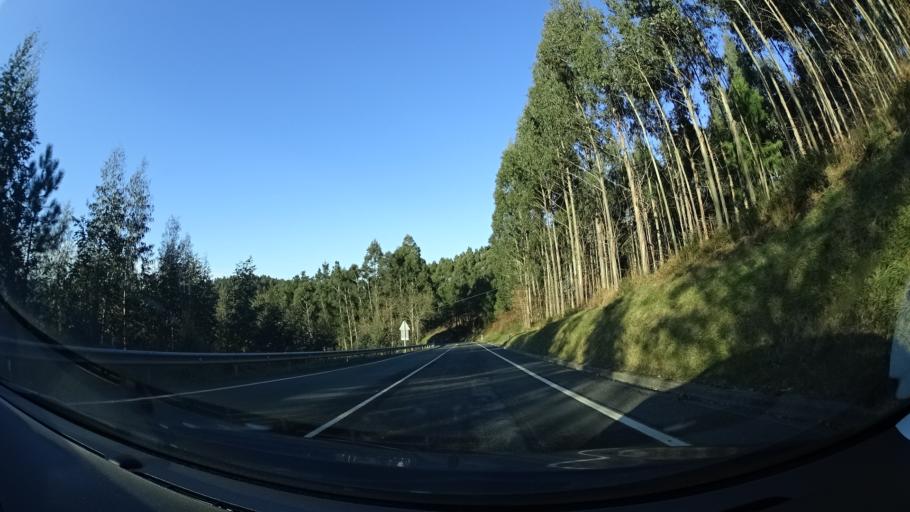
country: ES
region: Basque Country
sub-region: Bizkaia
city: Bakio
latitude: 43.3853
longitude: -2.7781
